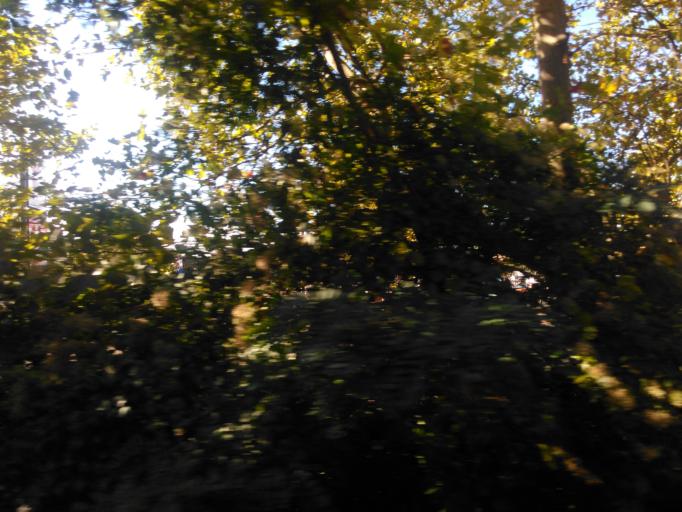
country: DE
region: Berlin
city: Fennpfuhl
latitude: 52.5238
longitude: 13.4639
